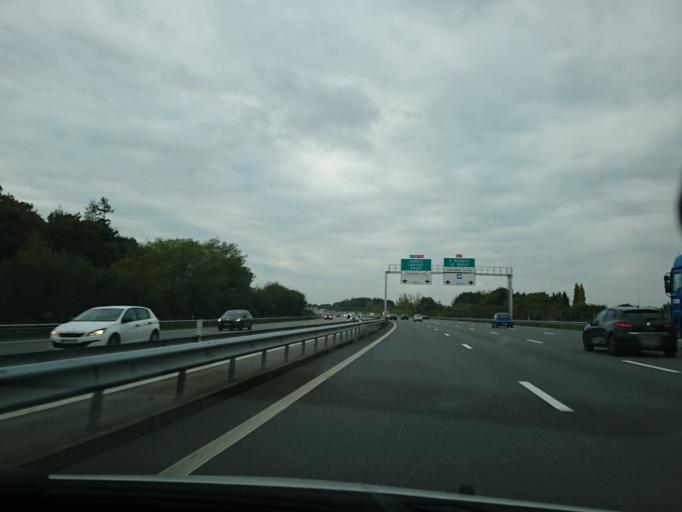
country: FR
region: Pays de la Loire
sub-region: Departement de la Loire-Atlantique
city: Savenay
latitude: 47.3678
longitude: -1.9101
